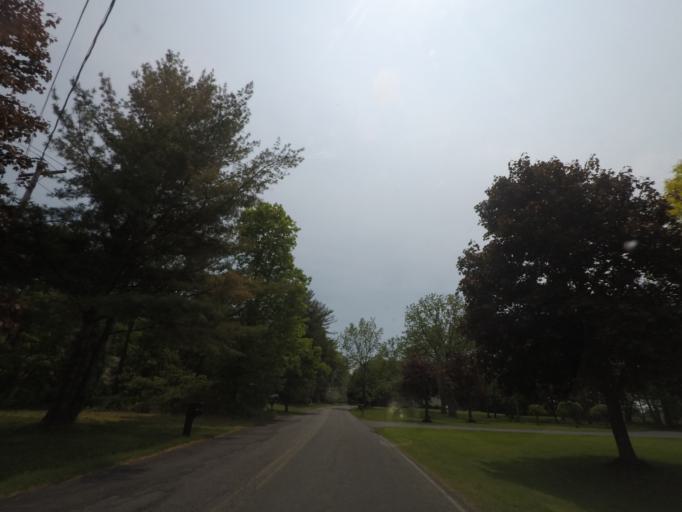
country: US
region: New York
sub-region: Rensselaer County
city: Castleton-on-Hudson
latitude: 42.5309
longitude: -73.7142
